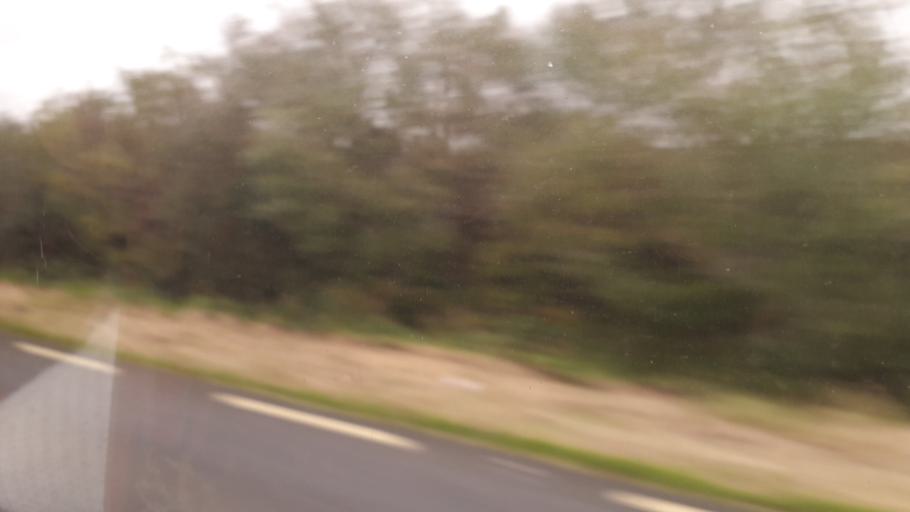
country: IE
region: Munster
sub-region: An Clar
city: Ennis
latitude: 52.8965
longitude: -9.2060
